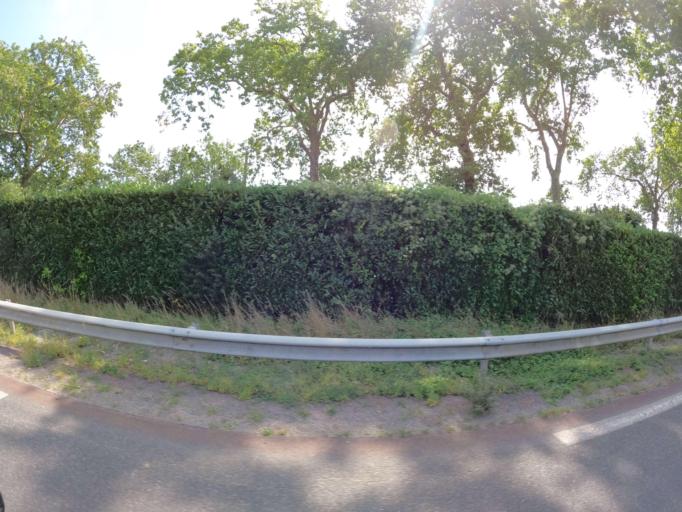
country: FR
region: Poitou-Charentes
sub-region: Departement des Deux-Sevres
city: Frontenay-Rohan-Rohan
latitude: 46.2645
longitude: -0.5309
